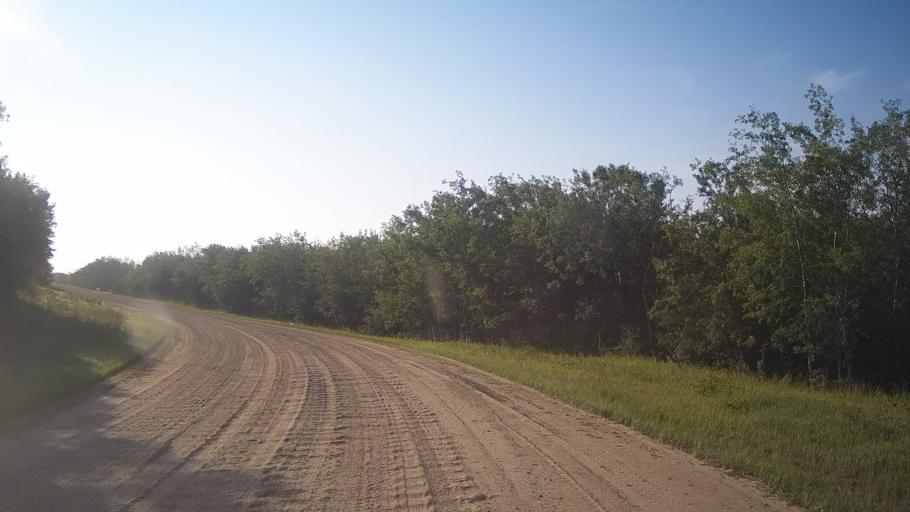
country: CA
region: Saskatchewan
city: Saskatoon
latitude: 51.8238
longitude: -106.5417
